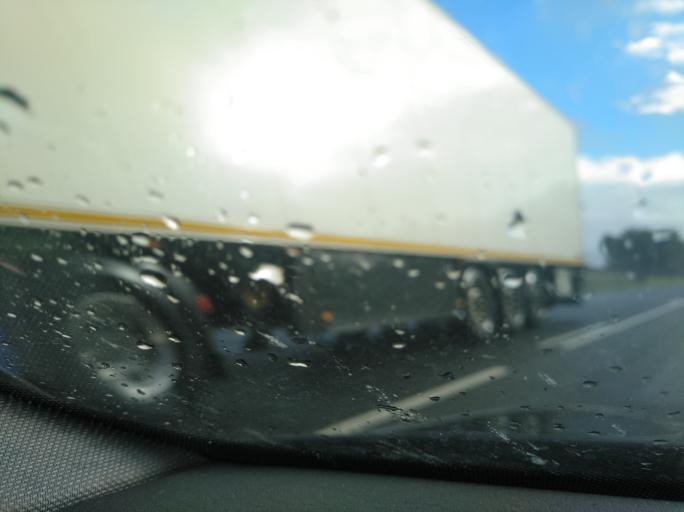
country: PT
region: Setubal
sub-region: Grandola
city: Grandola
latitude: 38.0450
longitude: -8.4016
